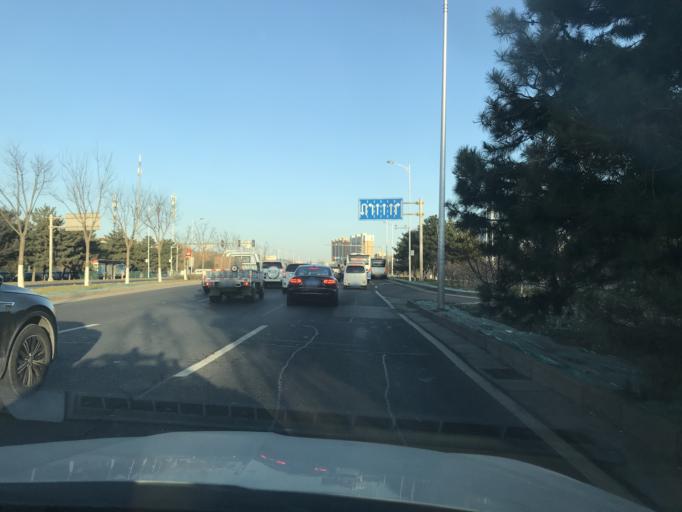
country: CN
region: Beijing
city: Xibeiwang
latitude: 40.0747
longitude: 116.2464
